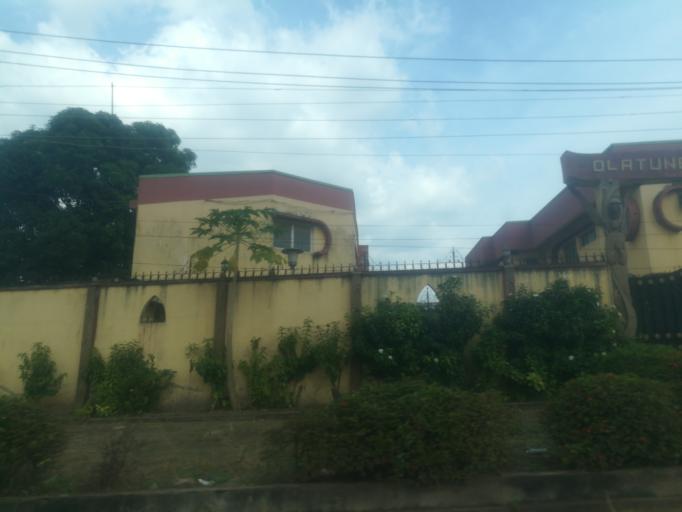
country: NG
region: Ogun
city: Abeokuta
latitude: 7.1257
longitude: 3.3212
